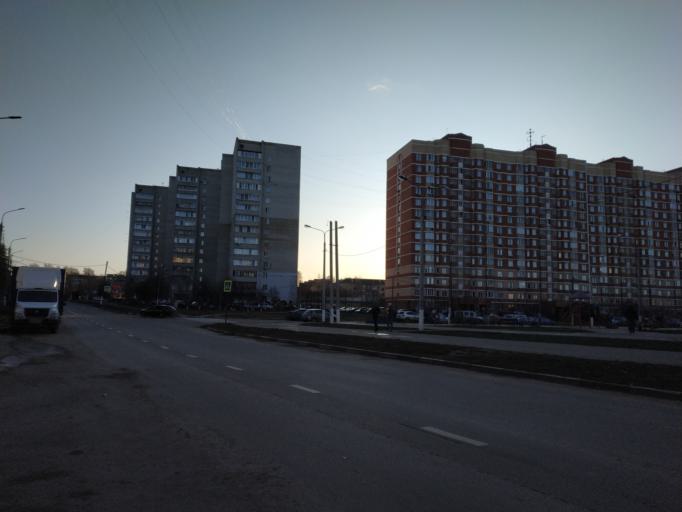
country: RU
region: Moskovskaya
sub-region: Podol'skiy Rayon
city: Podol'sk
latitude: 55.4042
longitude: 37.5616
